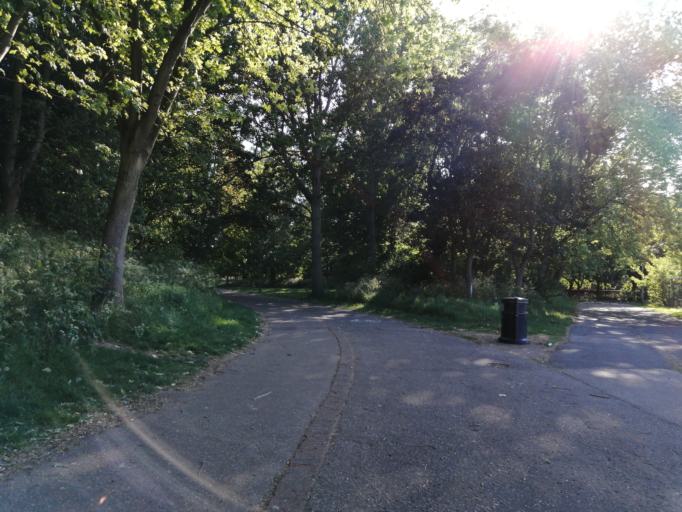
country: GB
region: England
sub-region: Peterborough
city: Marholm
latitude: 52.5996
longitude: -0.2812
